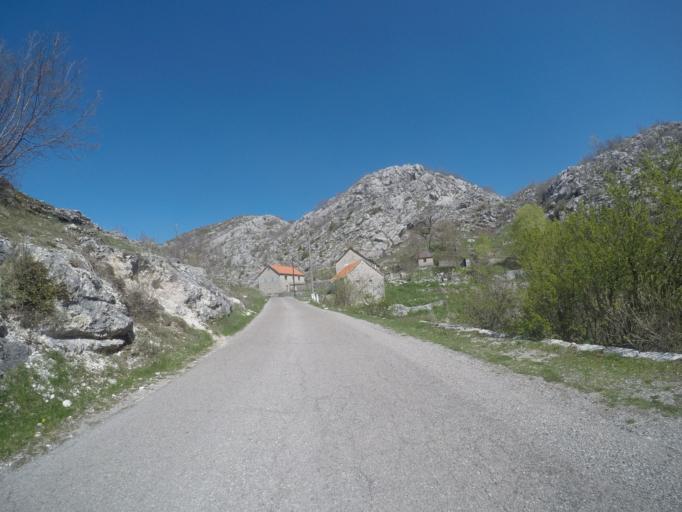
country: ME
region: Cetinje
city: Cetinje
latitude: 42.4579
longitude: 18.8732
